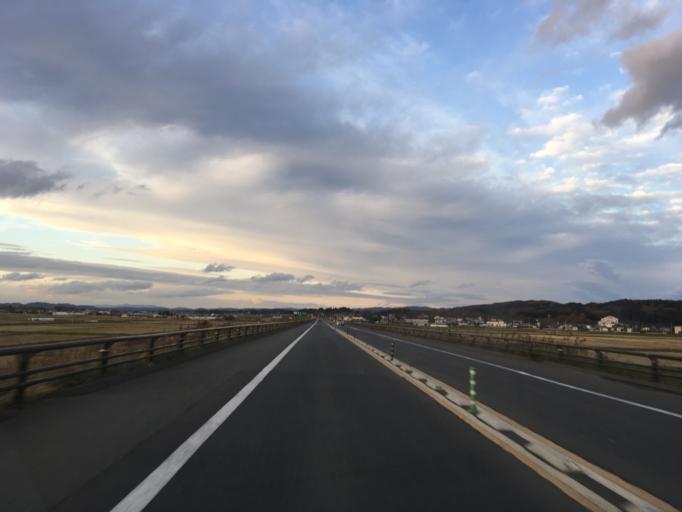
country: JP
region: Miyagi
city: Wakuya
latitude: 38.6541
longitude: 141.2641
